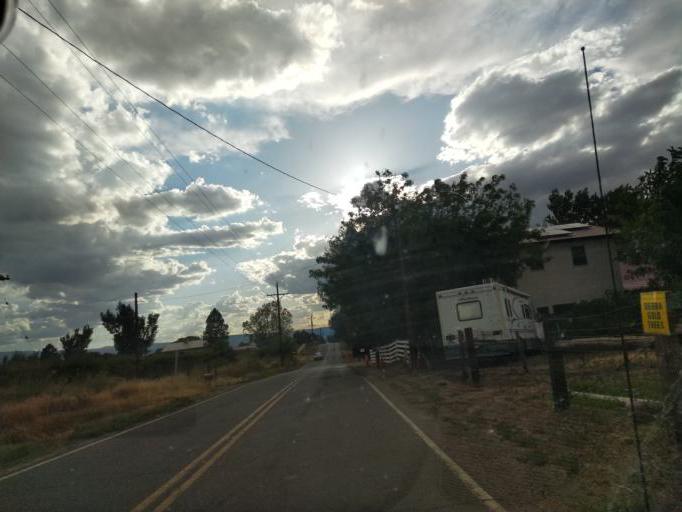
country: US
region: Colorado
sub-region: Mesa County
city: Clifton
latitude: 39.0558
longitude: -108.4191
